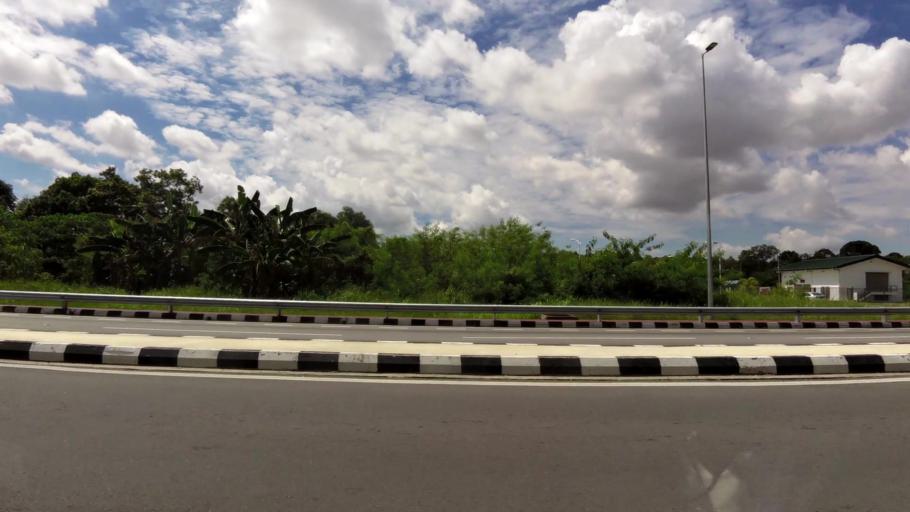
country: BN
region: Brunei and Muara
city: Bandar Seri Begawan
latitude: 4.9393
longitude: 114.9037
